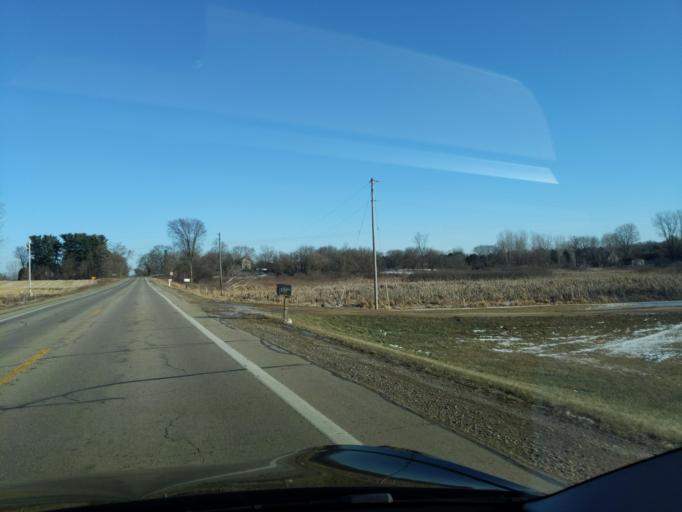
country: US
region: Michigan
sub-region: Ingham County
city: Stockbridge
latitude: 42.3937
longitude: -84.2616
